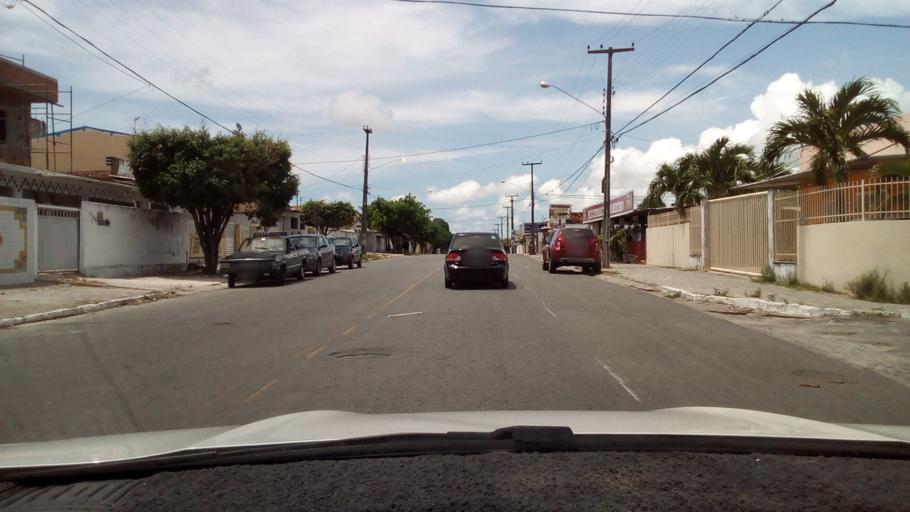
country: BR
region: Paraiba
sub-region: Joao Pessoa
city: Joao Pessoa
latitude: -7.1831
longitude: -34.8471
